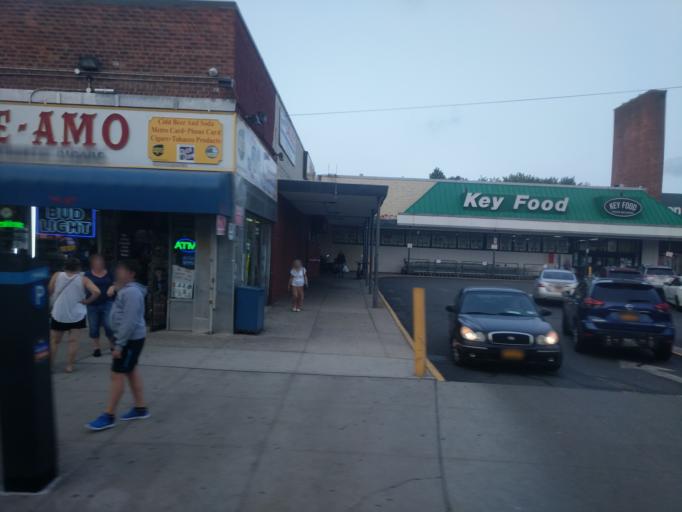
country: US
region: New York
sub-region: Queens County
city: Jamaica
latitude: 40.7182
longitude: -73.8171
